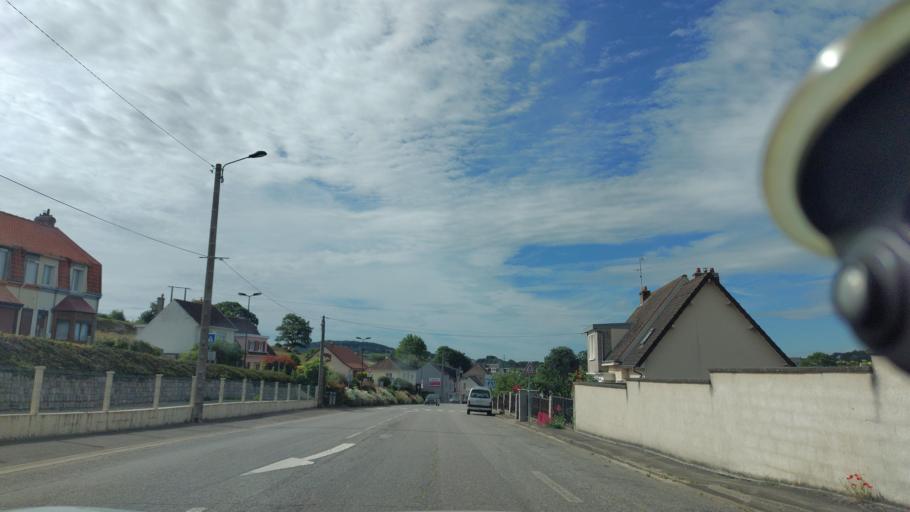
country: FR
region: Haute-Normandie
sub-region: Departement de la Seine-Maritime
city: Eu
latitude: 50.0592
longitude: 1.4244
